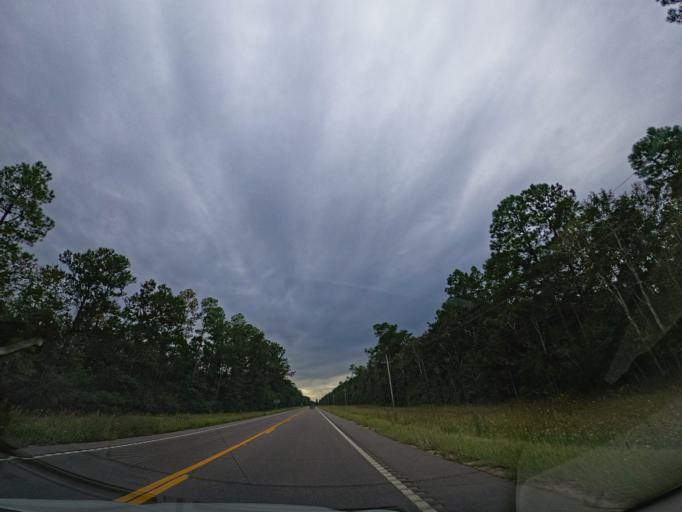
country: US
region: Mississippi
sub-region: Hancock County
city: Pearlington
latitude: 30.2673
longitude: -89.5611
